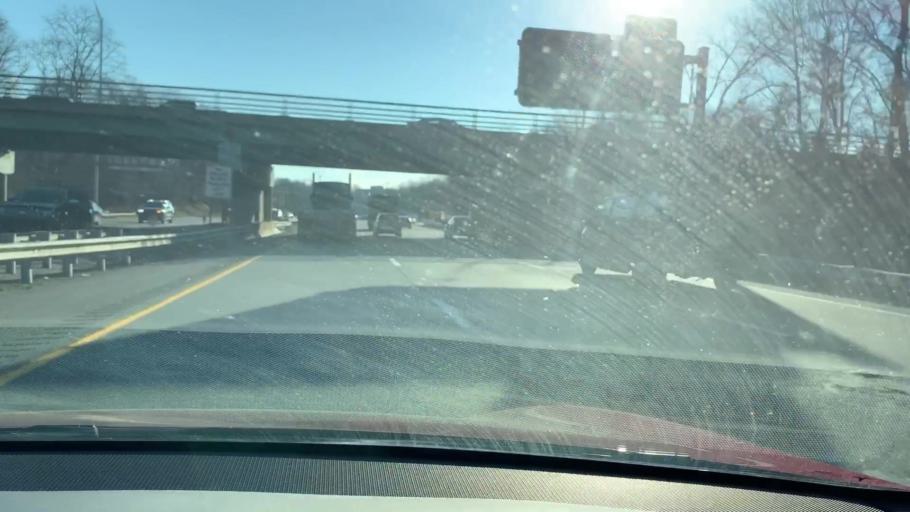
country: US
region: New York
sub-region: Westchester County
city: Purchase
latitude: 41.0283
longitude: -73.7367
